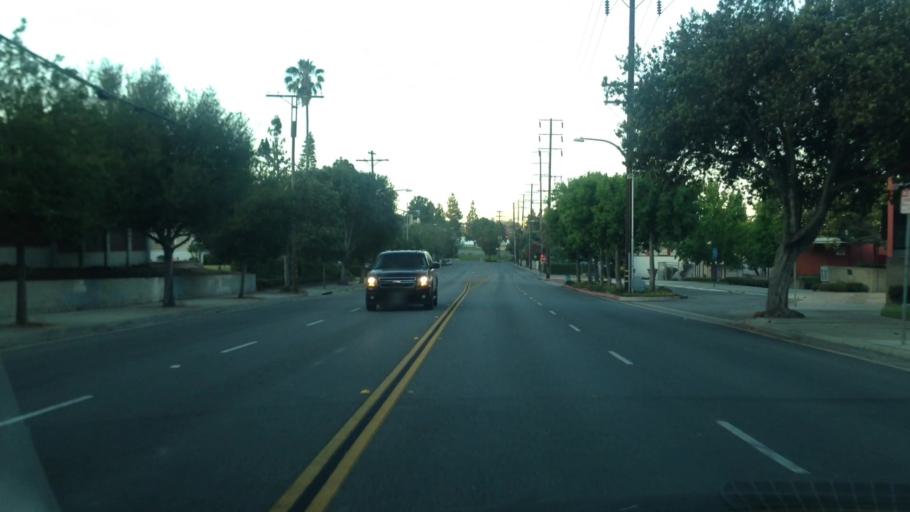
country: US
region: California
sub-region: Los Angeles County
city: Ladera Heights
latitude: 33.9966
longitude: -118.3904
